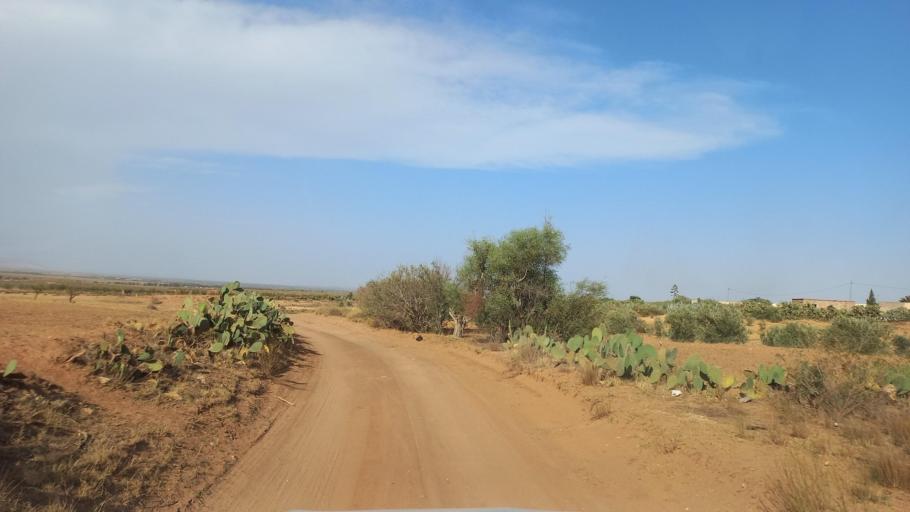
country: TN
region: Al Qasrayn
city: Kasserine
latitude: 35.2092
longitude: 8.9685
